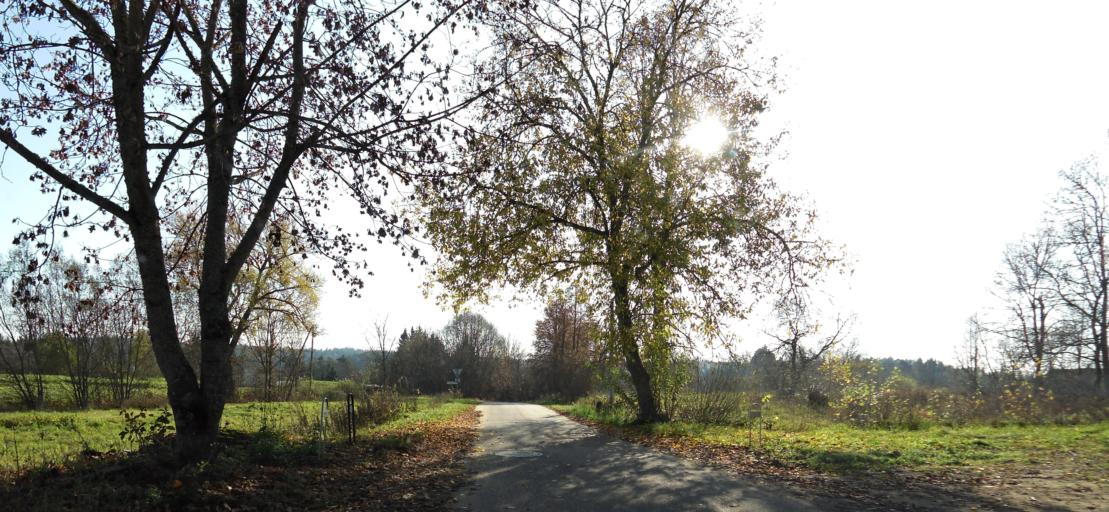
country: LT
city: Aukstadvaris
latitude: 54.5761
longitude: 24.5205
